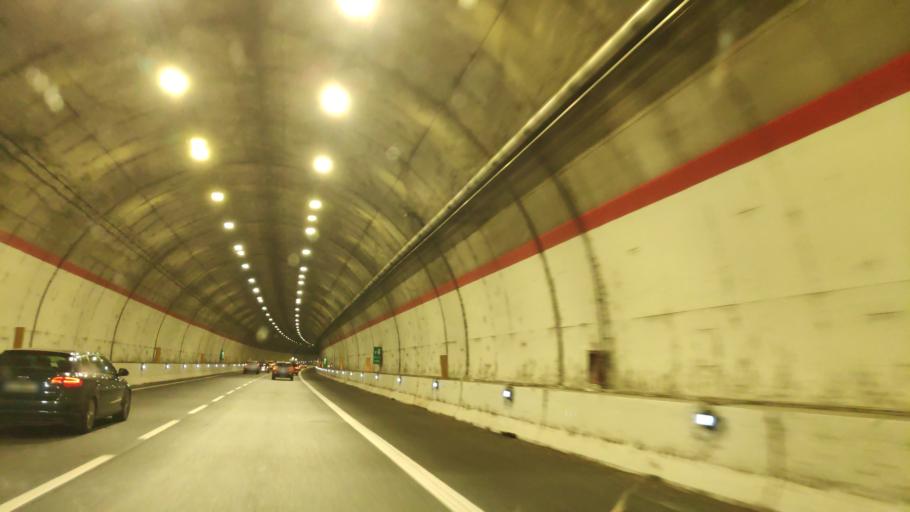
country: IT
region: Campania
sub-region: Provincia di Salerno
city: Sicignano degli Alburni
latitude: 40.6009
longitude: 15.3085
